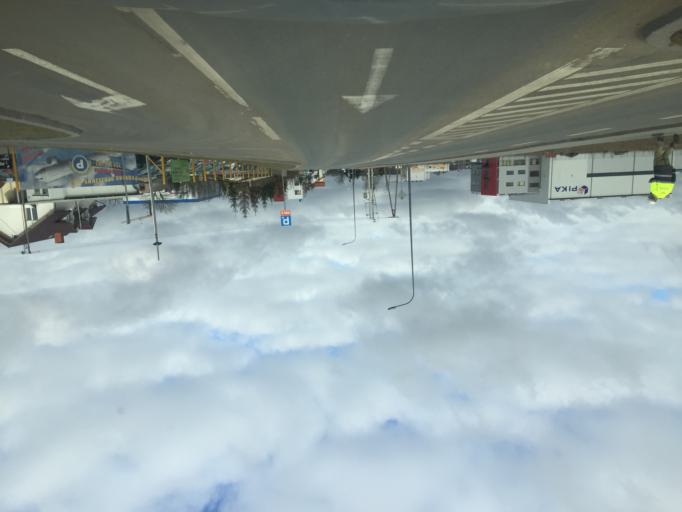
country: PL
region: Pomeranian Voivodeship
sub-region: Powiat kartuski
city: Banino
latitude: 54.3839
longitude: 18.4692
